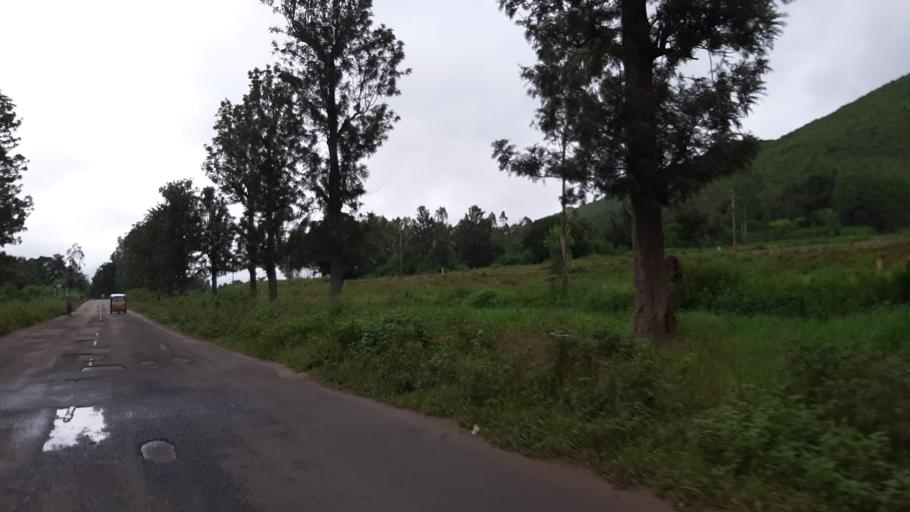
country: IN
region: Andhra Pradesh
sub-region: Vizianagaram District
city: Salur
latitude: 18.2912
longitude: 82.9231
